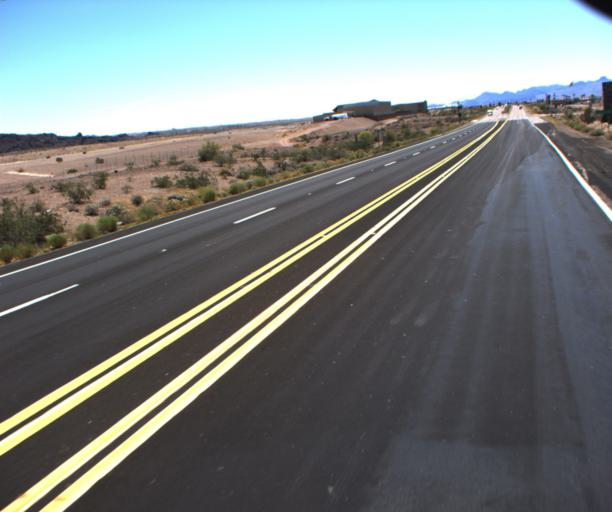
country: US
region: Arizona
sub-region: Mohave County
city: Desert Hills
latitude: 34.5815
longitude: -114.3678
